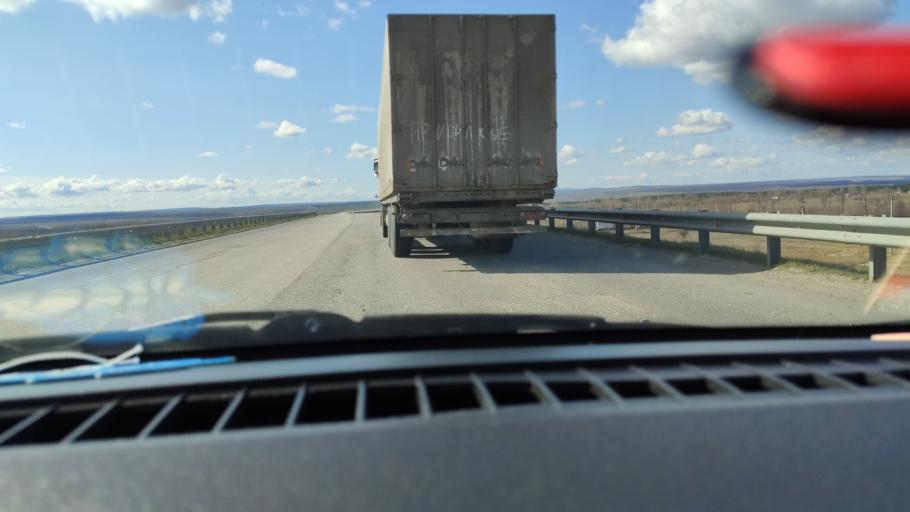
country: RU
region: Samara
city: Varlamovo
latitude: 53.1737
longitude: 48.2816
